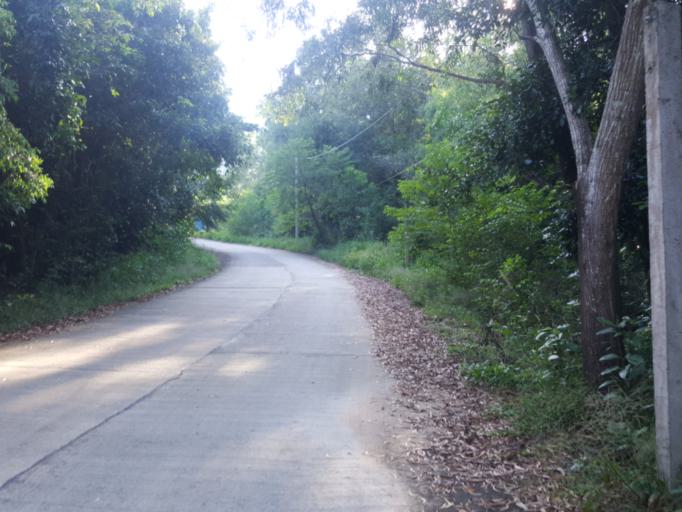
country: VN
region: Kien Giang
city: Duong GJong
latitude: 10.0576
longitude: 104.0327
